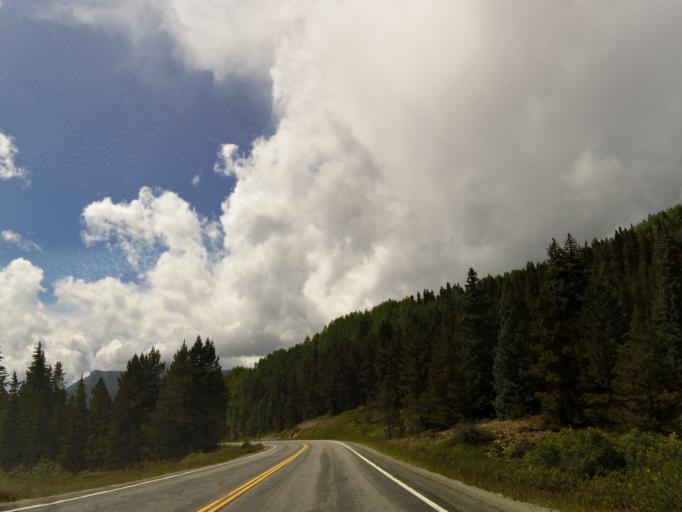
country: US
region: Colorado
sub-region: San Juan County
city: Silverton
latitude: 37.7326
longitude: -107.7197
